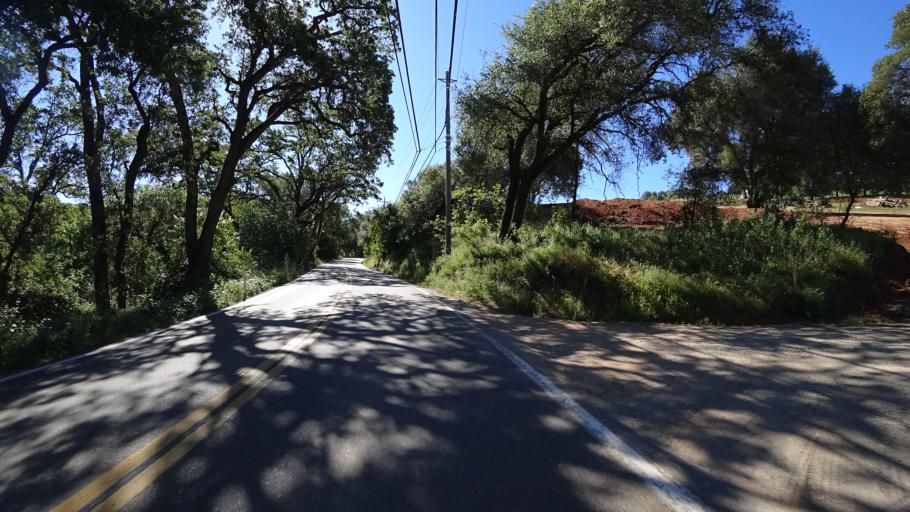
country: US
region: California
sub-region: Placer County
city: Newcastle
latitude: 38.8786
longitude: -121.1686
